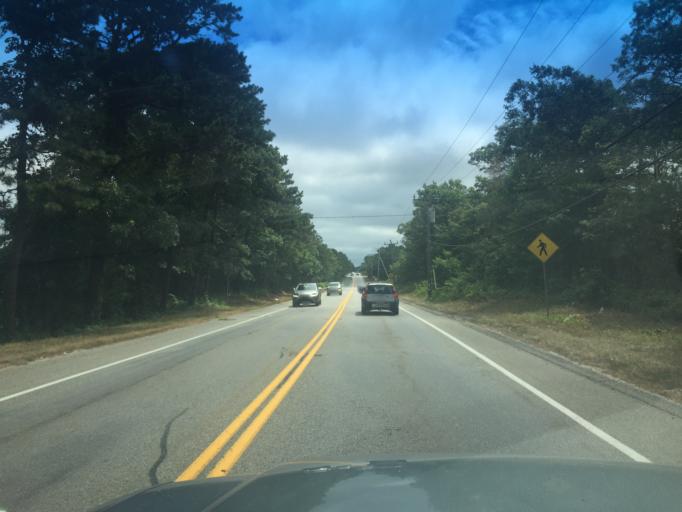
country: US
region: Massachusetts
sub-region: Barnstable County
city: East Falmouth
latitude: 41.6187
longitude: -70.5390
